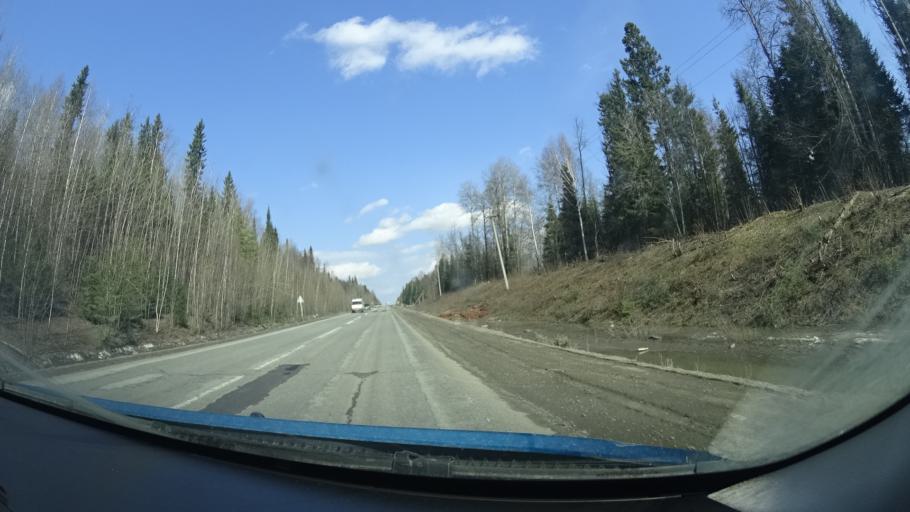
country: RU
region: Perm
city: Kultayevo
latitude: 57.8107
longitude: 55.7902
